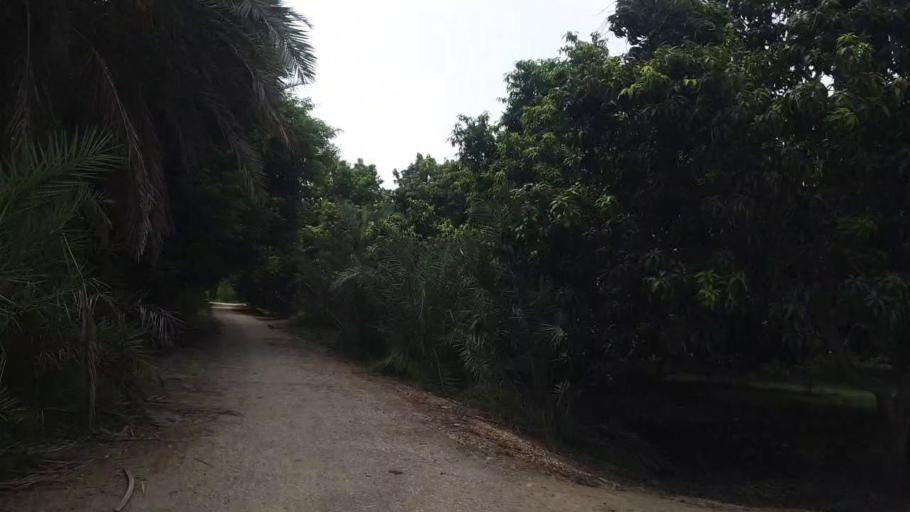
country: PK
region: Sindh
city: Pir jo Goth
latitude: 27.6112
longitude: 68.6756
